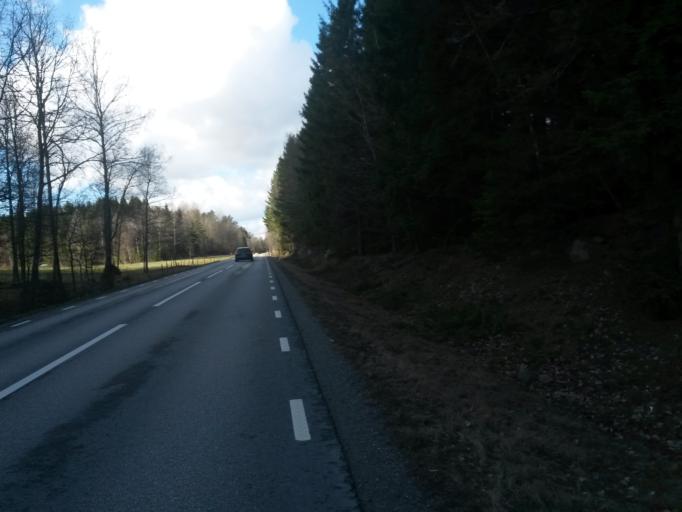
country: SE
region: Vaestra Goetaland
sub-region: Vargarda Kommun
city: Jonstorp
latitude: 58.0617
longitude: 12.7176
